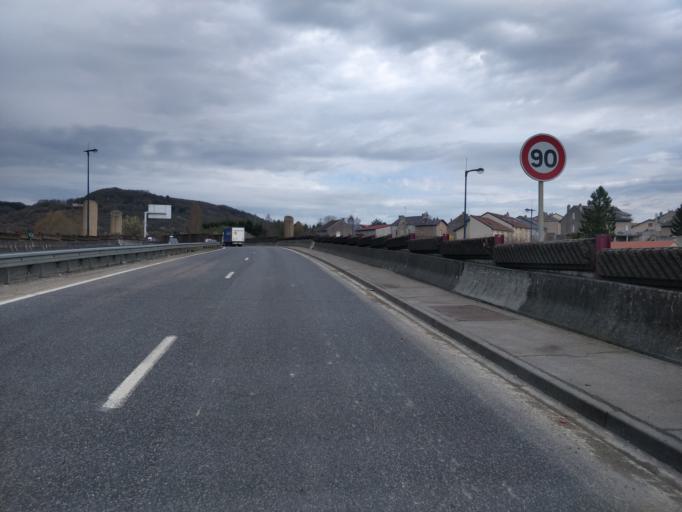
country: FR
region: Lorraine
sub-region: Departement de la Moselle
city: Vitry-sur-Orne
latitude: 49.2644
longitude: 6.1098
